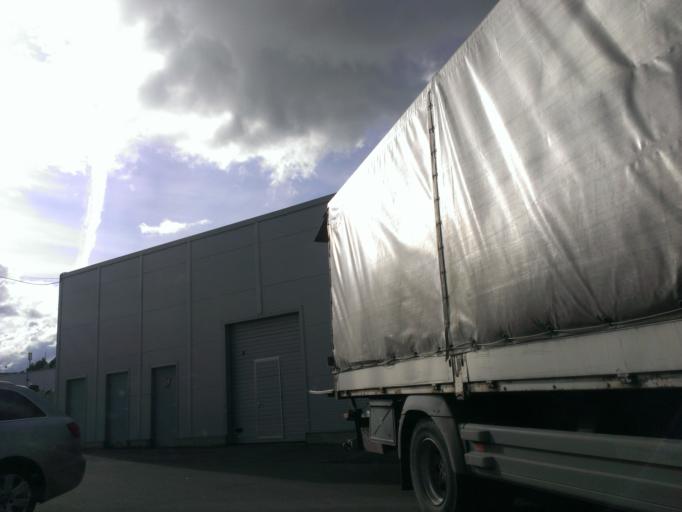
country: LV
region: Stopini
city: Ulbroka
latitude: 56.9541
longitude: 24.2204
